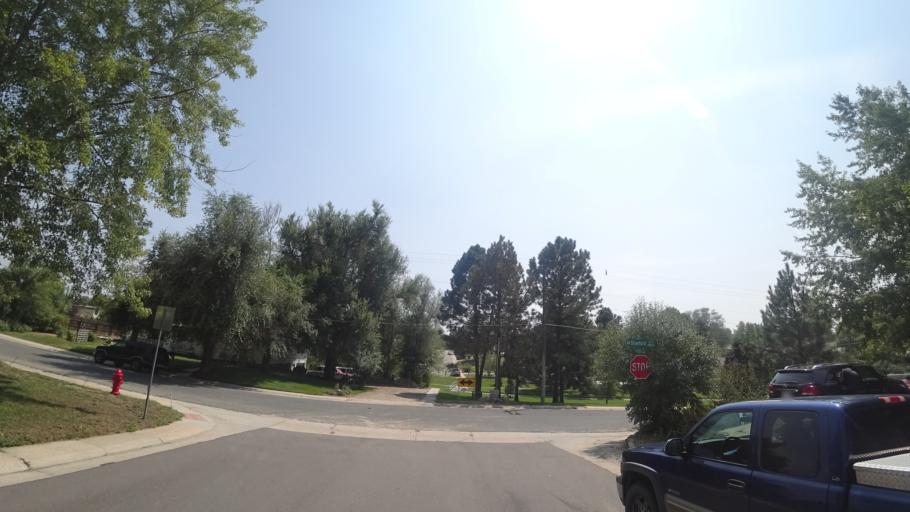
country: US
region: Colorado
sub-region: Arapahoe County
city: Englewood
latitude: 39.6351
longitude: -104.9938
